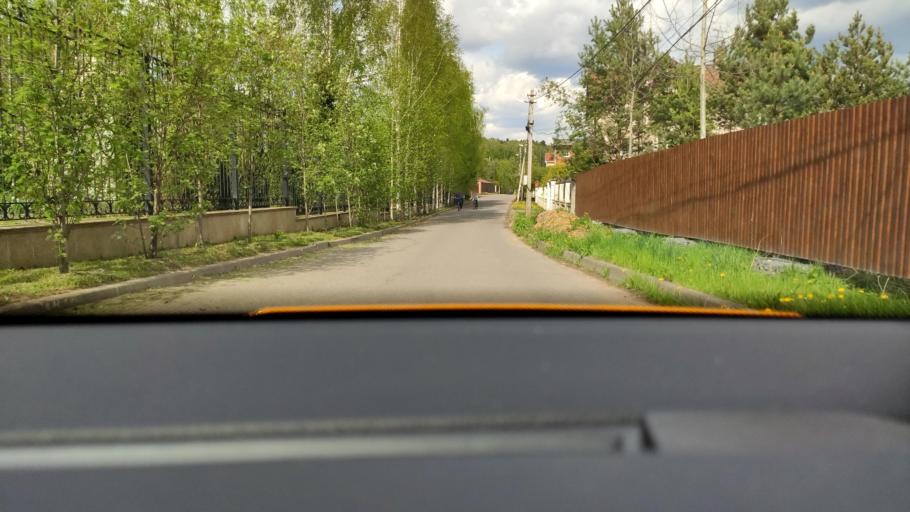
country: RU
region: Moskovskaya
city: Nikolina Gora
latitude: 55.7434
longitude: 37.0024
